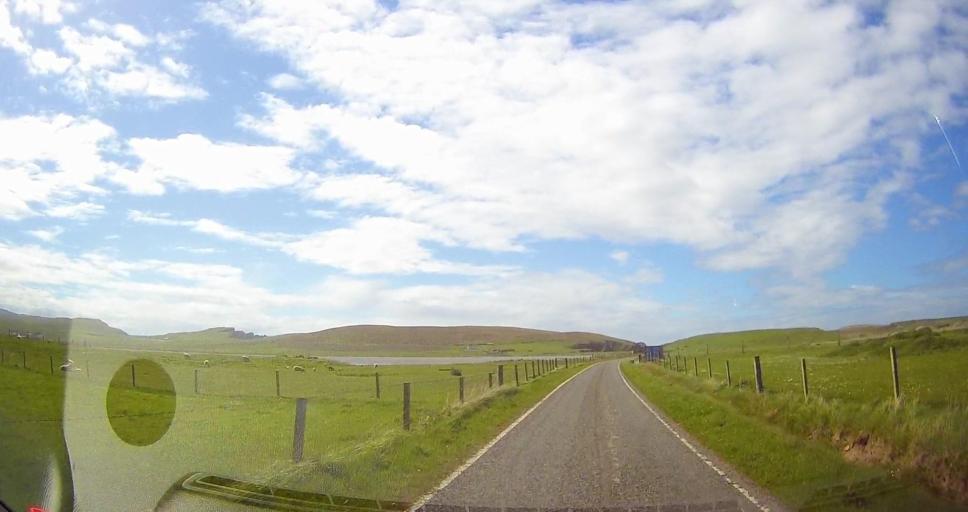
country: GB
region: Scotland
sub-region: Shetland Islands
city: Sandwick
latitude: 59.9410
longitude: -1.3302
